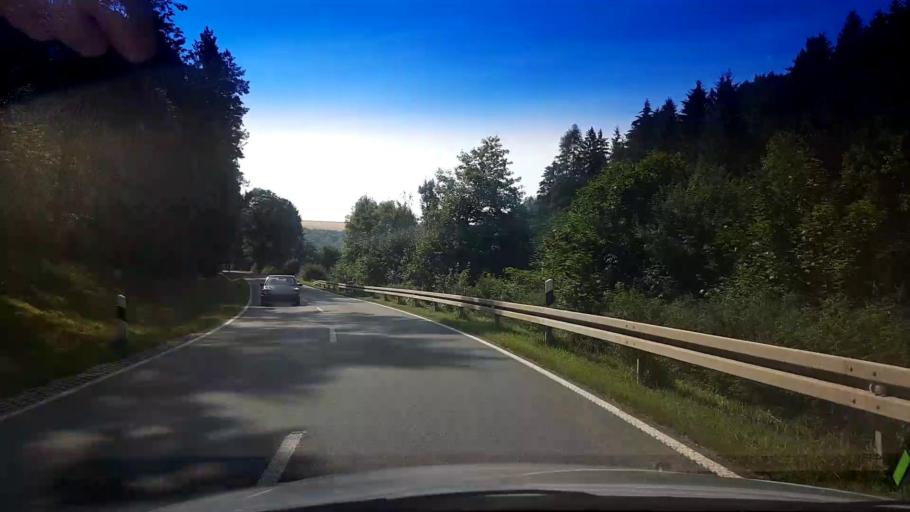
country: DE
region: Bavaria
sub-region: Upper Franconia
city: Hollfeld
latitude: 49.9407
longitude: 11.3387
